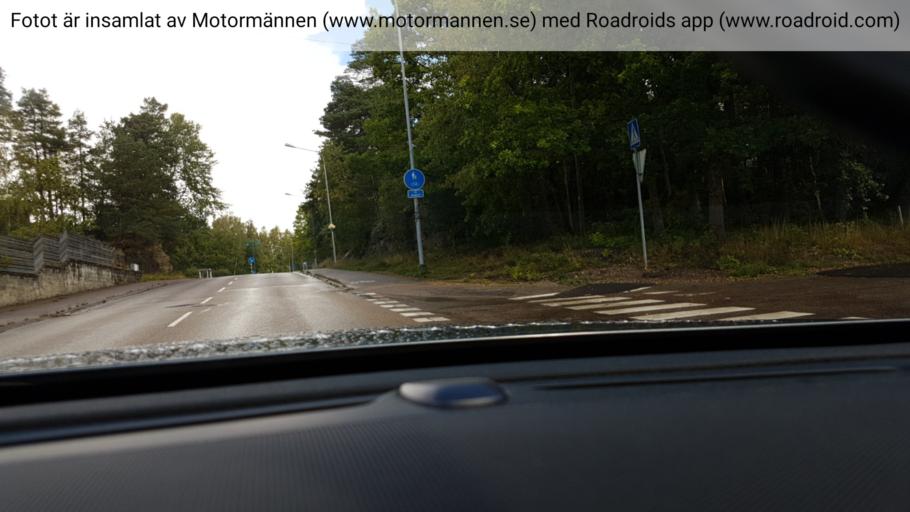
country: SE
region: Vaestra Goetaland
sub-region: Vanersborgs Kommun
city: Vanersborg
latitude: 58.3684
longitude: 12.2845
